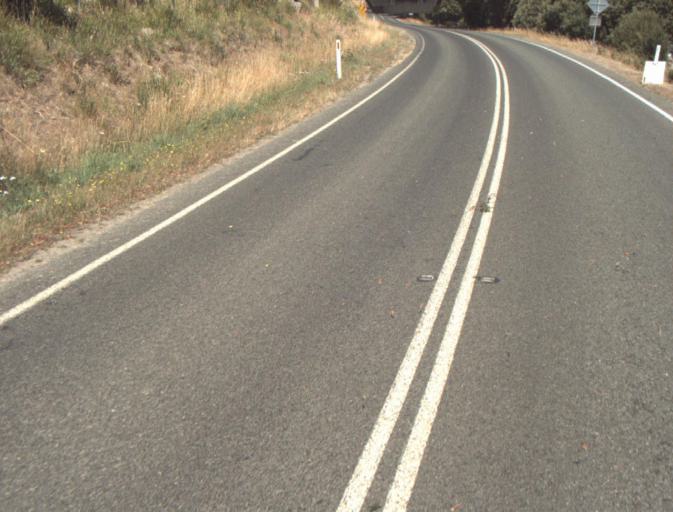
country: AU
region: Tasmania
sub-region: Launceston
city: Newstead
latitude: -41.3251
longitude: 147.3573
